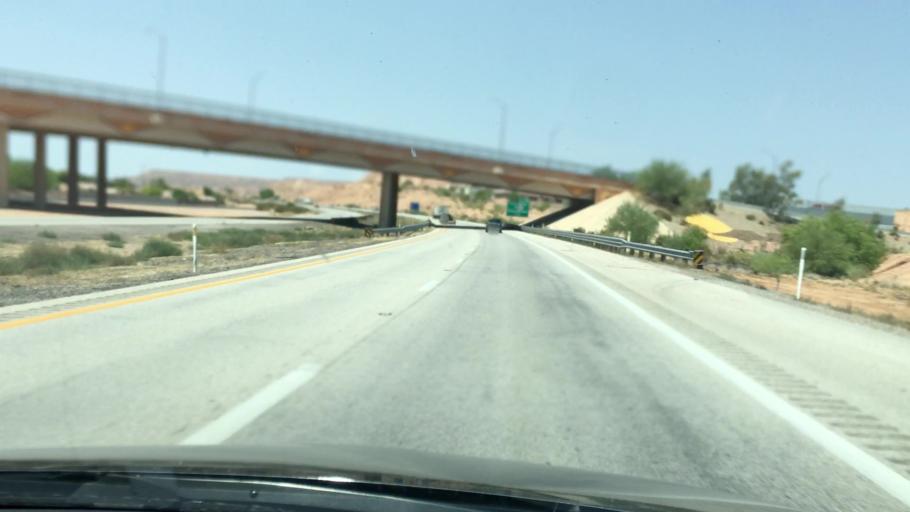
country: US
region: Nevada
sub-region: Clark County
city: Mesquite
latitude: 36.8100
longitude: -114.0850
